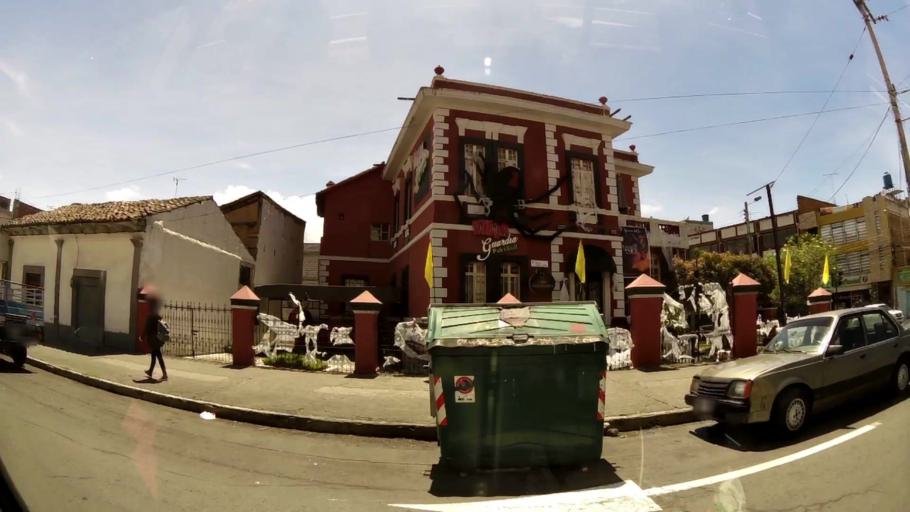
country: EC
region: Chimborazo
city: Riobamba
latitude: -1.6687
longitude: -78.6558
